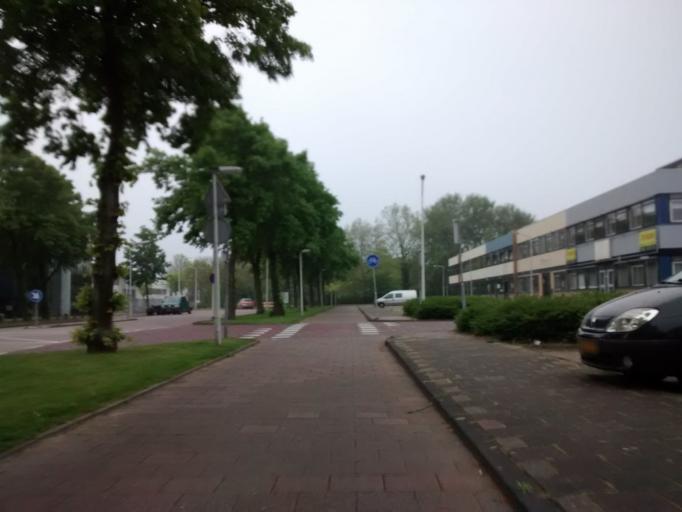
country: NL
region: South Holland
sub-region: Gemeente Leiderdorp
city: Leiderdorp
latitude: 52.1599
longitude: 4.5115
